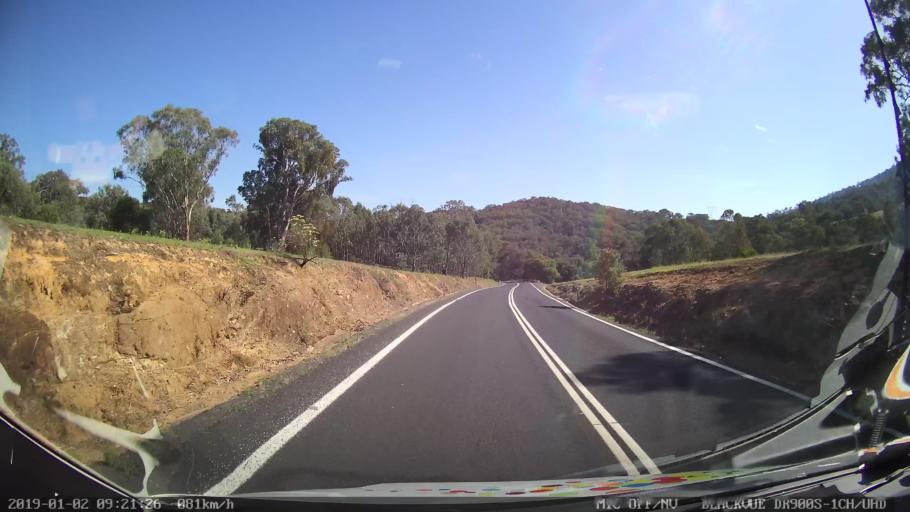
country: AU
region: New South Wales
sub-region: Tumut Shire
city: Tumut
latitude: -35.4058
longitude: 148.2913
